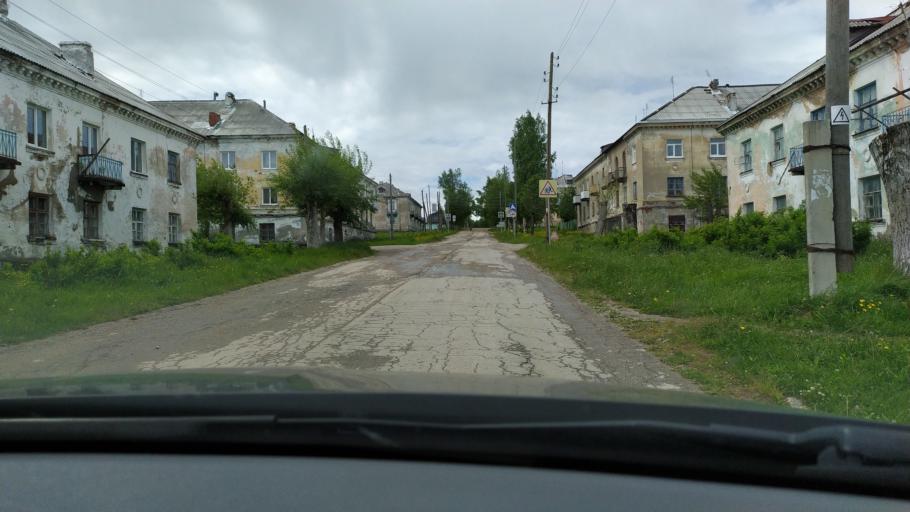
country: RU
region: Perm
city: Gremyachinsk
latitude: 58.5109
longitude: 57.8328
